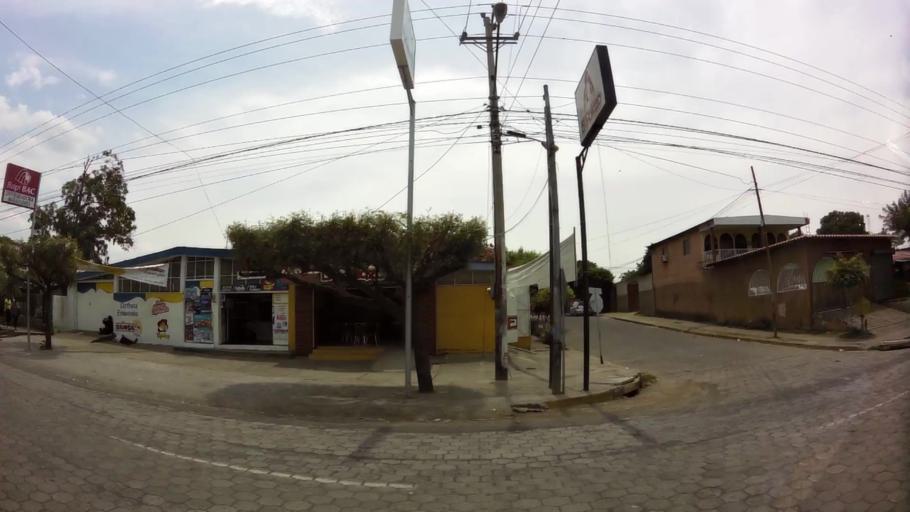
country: NI
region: Managua
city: Ciudad Sandino
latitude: 12.1456
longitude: -86.3049
